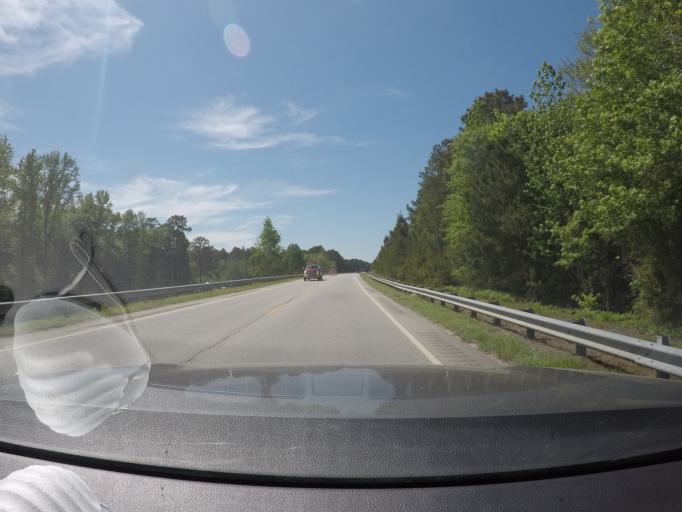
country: US
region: Georgia
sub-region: Evans County
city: Claxton
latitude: 32.1482
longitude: -81.7791
